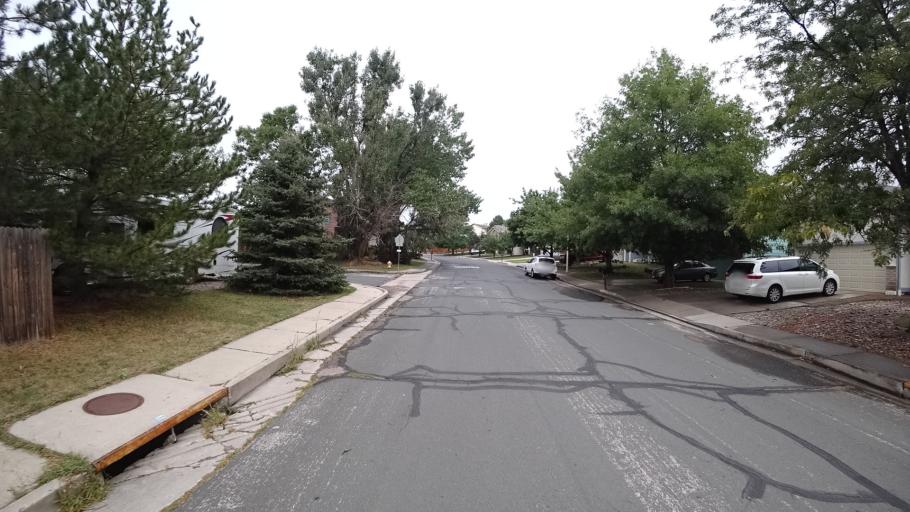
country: US
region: Colorado
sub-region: El Paso County
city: Cimarron Hills
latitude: 38.9217
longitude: -104.7506
